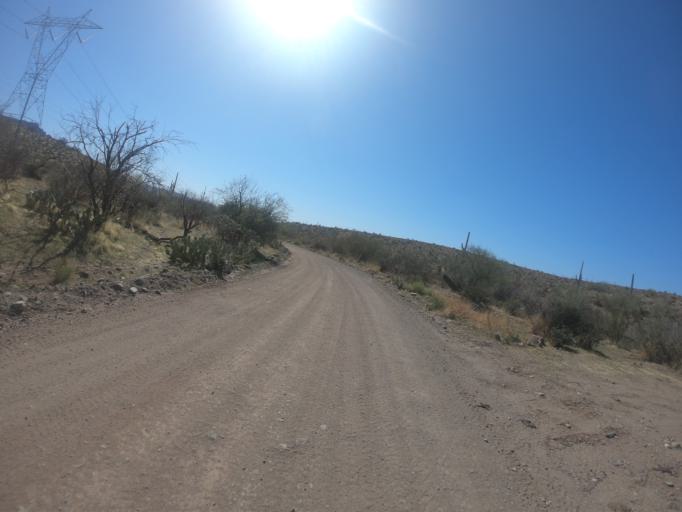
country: US
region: Arizona
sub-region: Pinal County
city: Superior
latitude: 33.2966
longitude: -111.1465
